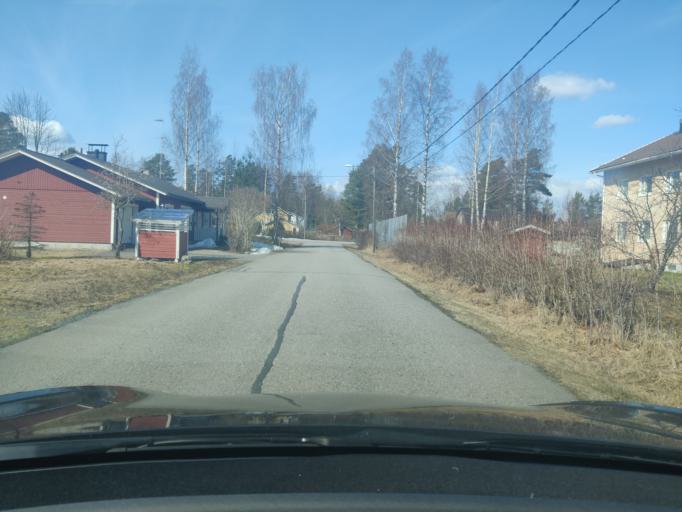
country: FI
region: Northern Savo
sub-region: Kuopio
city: Vehmersalmi
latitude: 62.9126
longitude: 28.1636
